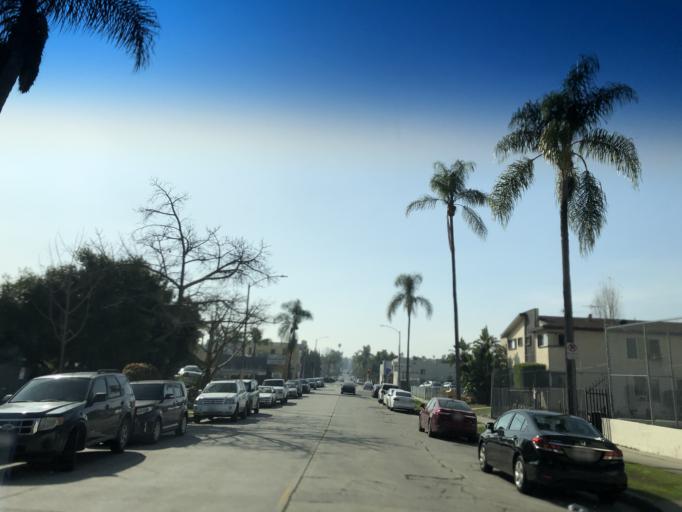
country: US
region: California
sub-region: Los Angeles County
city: Hollywood
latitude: 34.0551
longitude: -118.3202
